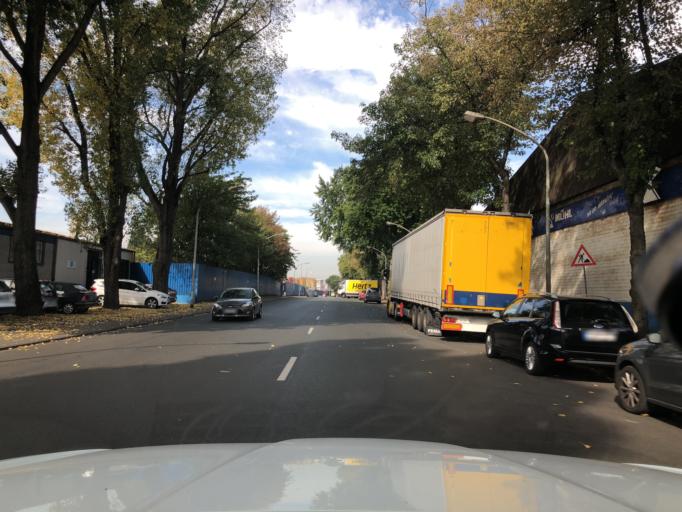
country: DE
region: North Rhine-Westphalia
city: Meiderich
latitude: 51.4582
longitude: 6.7907
